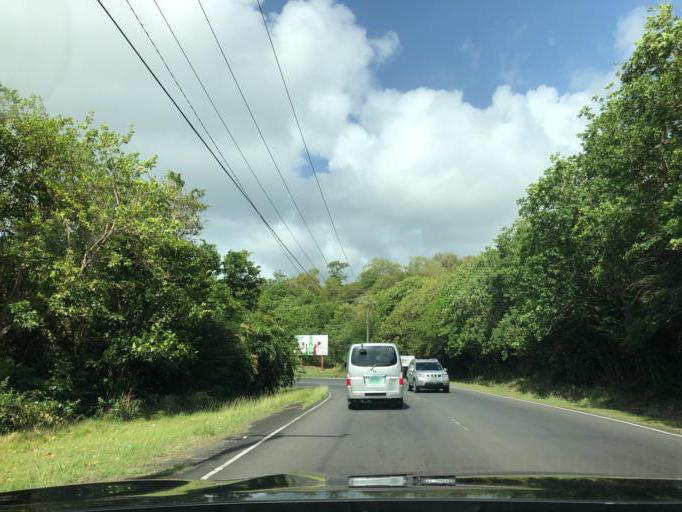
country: LC
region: Dennery Quarter
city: Dennery
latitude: 13.9214
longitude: -60.8971
